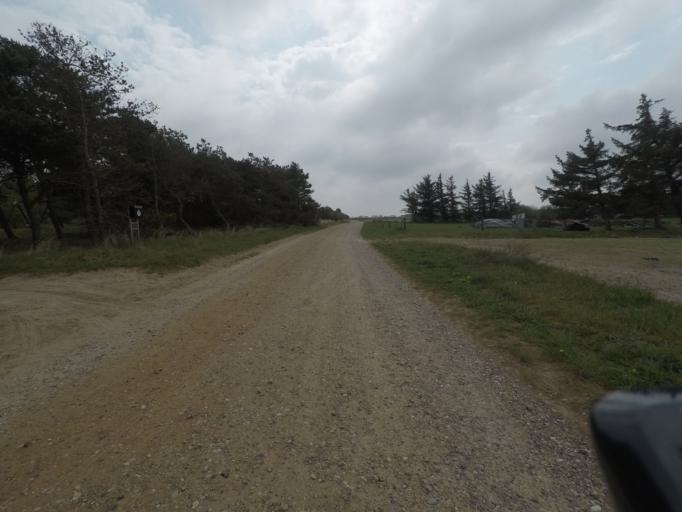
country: DE
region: Schleswig-Holstein
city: List
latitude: 55.0907
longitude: 8.5217
